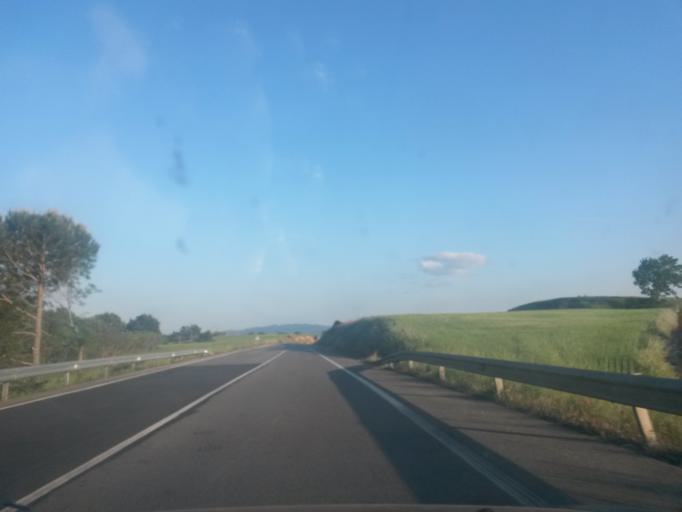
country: ES
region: Catalonia
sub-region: Provincia de Girona
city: Fontcoberta
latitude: 42.1129
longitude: 2.7915
